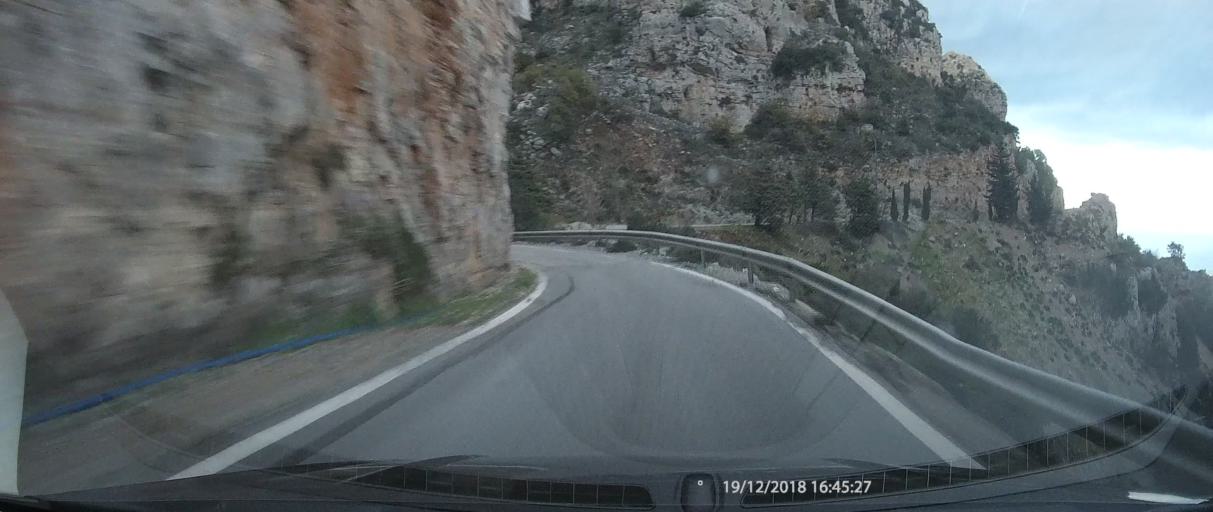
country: GR
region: Peloponnese
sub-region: Nomos Lakonias
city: Sykea
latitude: 36.9187
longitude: 23.0038
